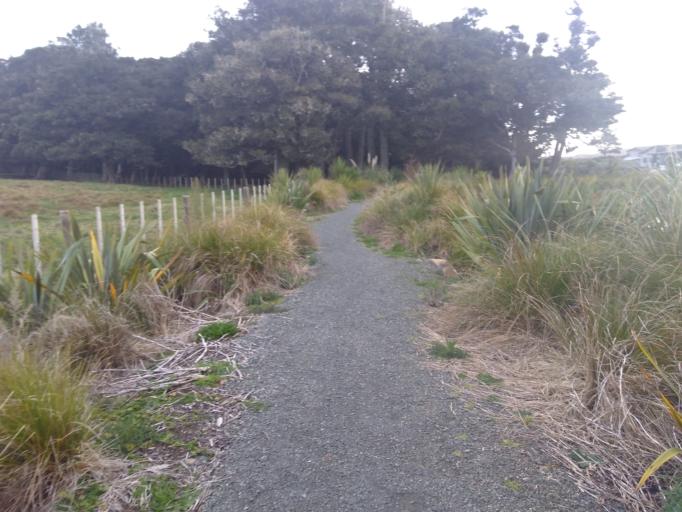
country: NZ
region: Northland
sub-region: Whangarei
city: Whangarei
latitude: -35.6961
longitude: 174.2643
